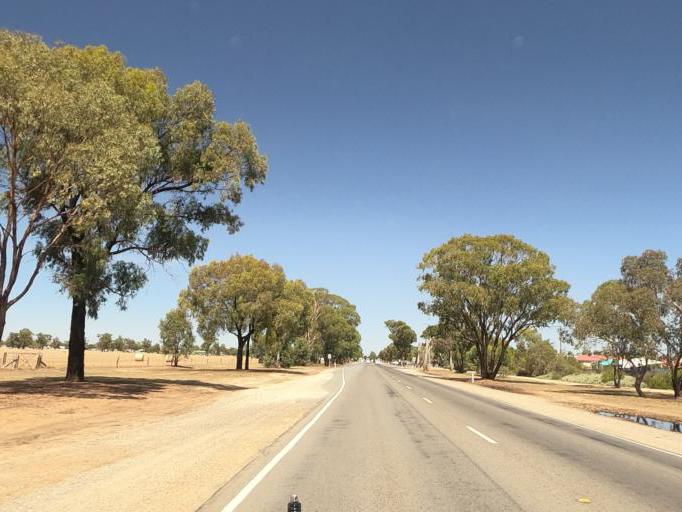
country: AU
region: Victoria
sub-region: Moira
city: Yarrawonga
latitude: -36.0122
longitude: 146.0227
